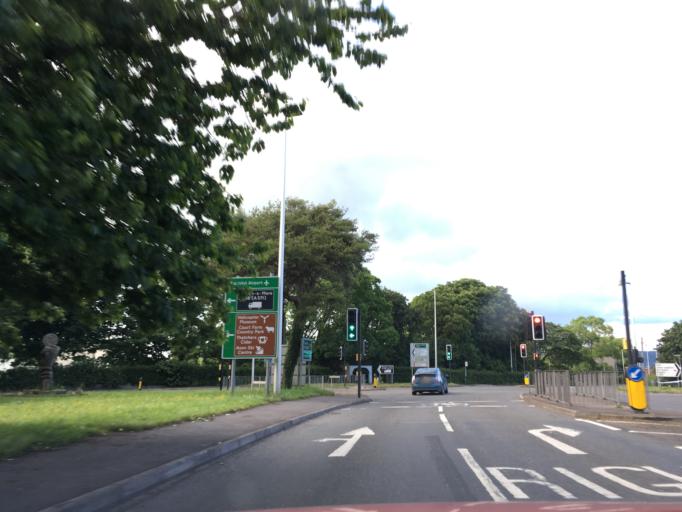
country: GB
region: England
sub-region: North Somerset
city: Churchill
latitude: 51.3342
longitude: -2.7941
